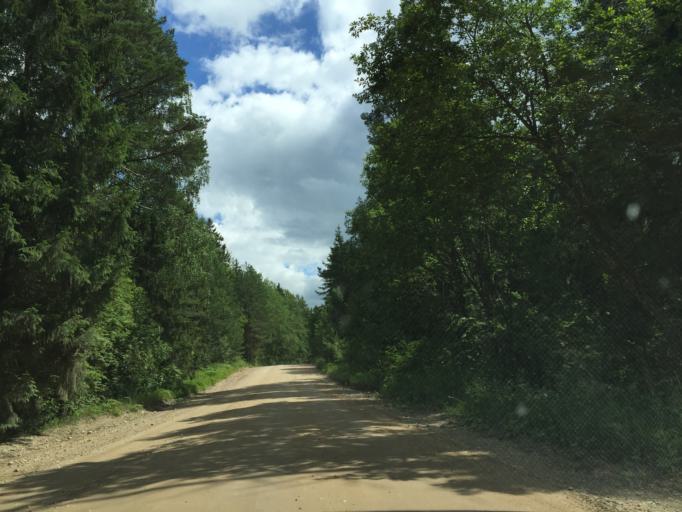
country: LV
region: Ropazu
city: Ropazi
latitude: 56.9147
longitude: 24.7496
